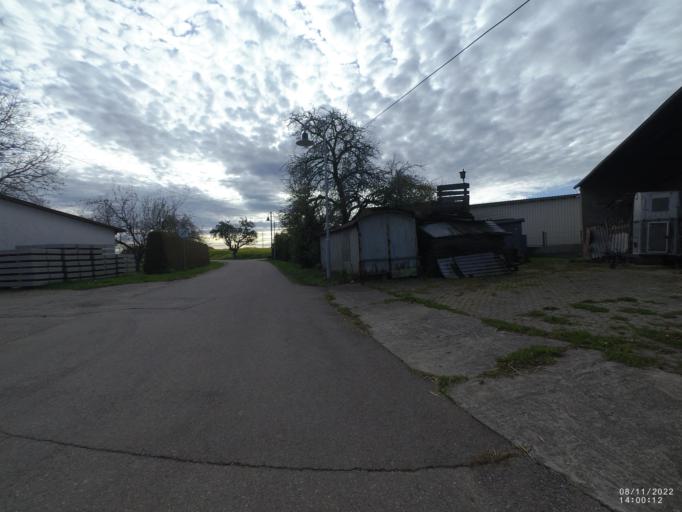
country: DE
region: Baden-Wuerttemberg
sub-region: Regierungsbezirk Stuttgart
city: Bad Uberkingen
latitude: 48.5820
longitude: 9.8028
